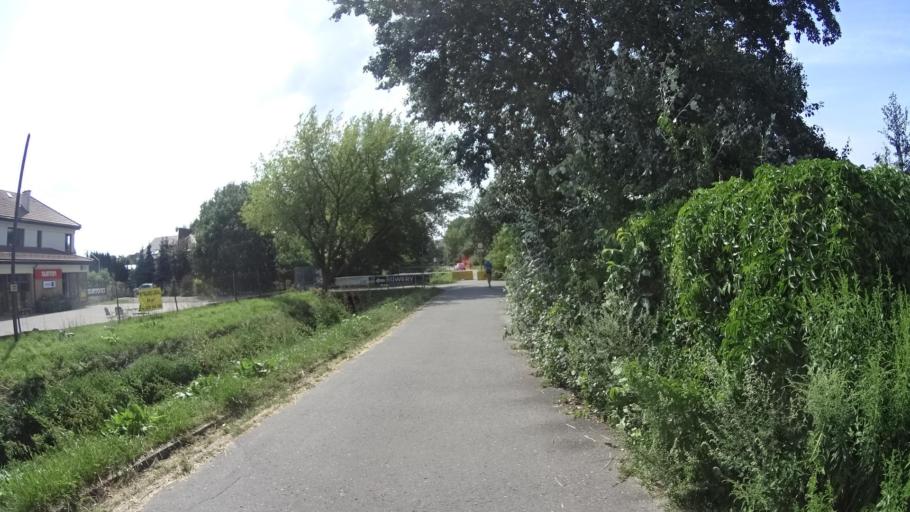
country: PL
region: Masovian Voivodeship
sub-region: Warszawa
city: Ursynow
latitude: 52.1700
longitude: 21.0630
